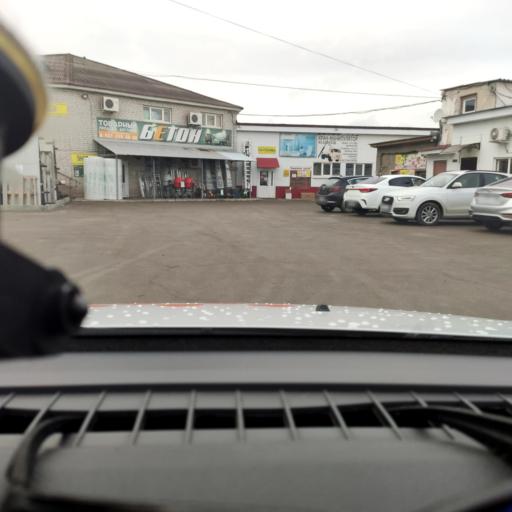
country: RU
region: Samara
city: Chapayevsk
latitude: 52.9724
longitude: 49.7118
